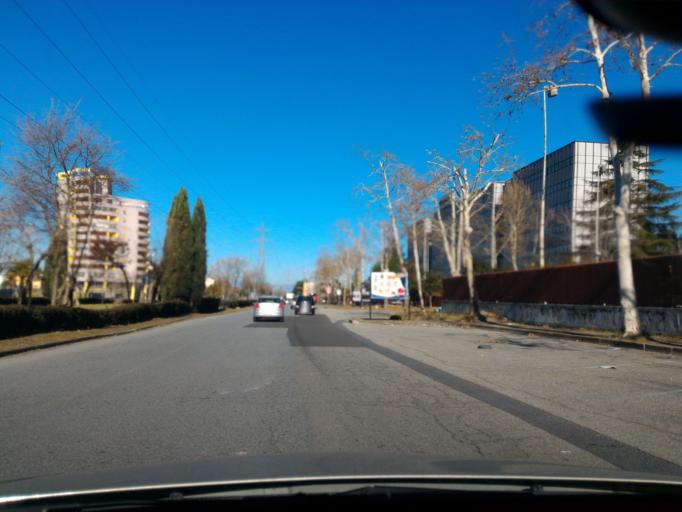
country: IT
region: Calabria
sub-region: Provincia di Cosenza
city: Cosenza
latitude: 39.3200
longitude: 16.2573
